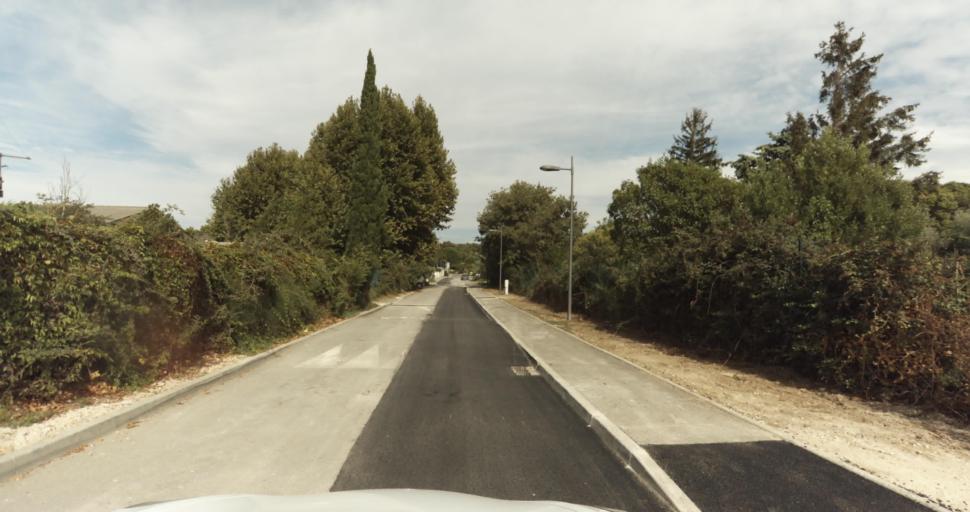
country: FR
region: Provence-Alpes-Cote d'Azur
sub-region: Departement des Bouches-du-Rhone
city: Miramas
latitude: 43.5716
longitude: 5.0164
